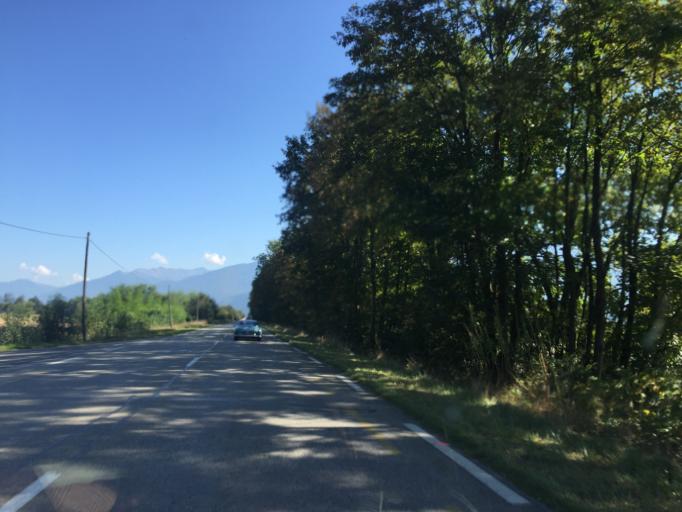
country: FR
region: Rhone-Alpes
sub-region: Departement de la Savoie
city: Aiton
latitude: 45.5656
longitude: 6.2087
